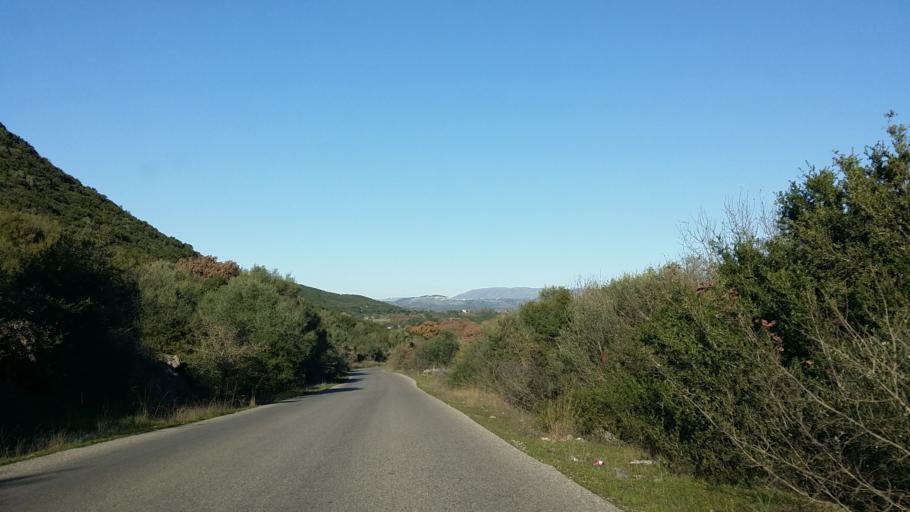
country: GR
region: West Greece
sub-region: Nomos Aitolias kai Akarnanias
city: Fitiai
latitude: 38.6135
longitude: 21.1407
